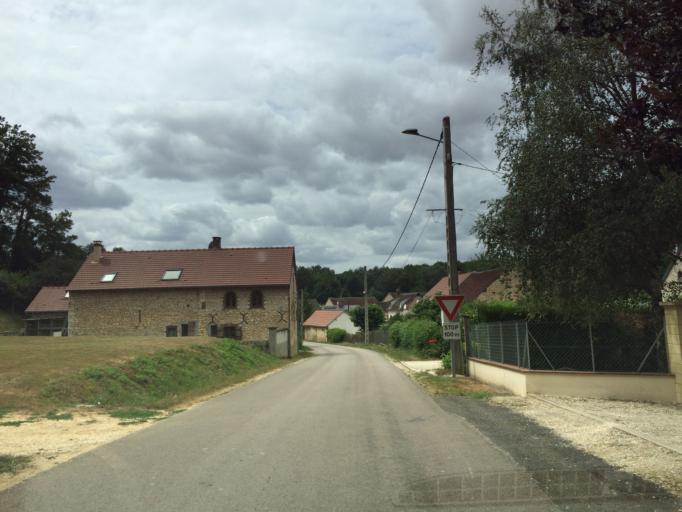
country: FR
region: Bourgogne
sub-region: Departement de l'Yonne
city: Fleury-la-Vallee
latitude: 47.8419
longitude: 3.4055
